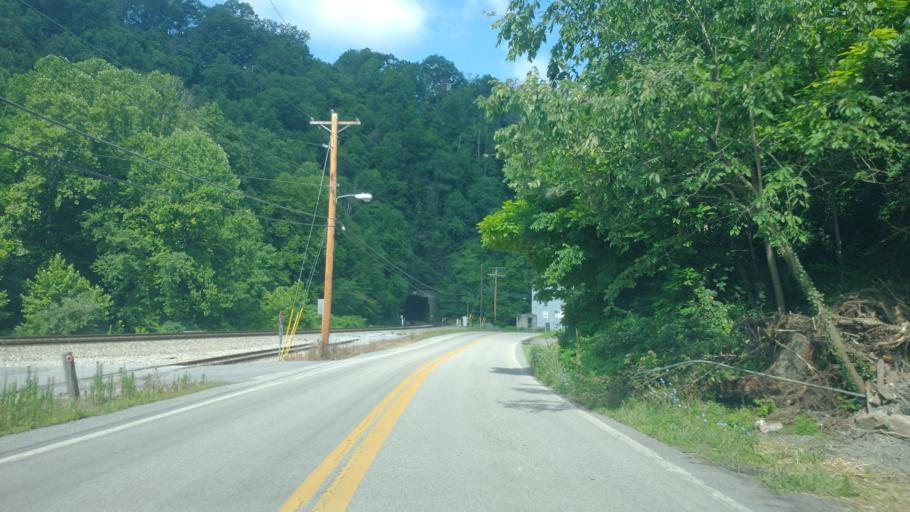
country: US
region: West Virginia
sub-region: McDowell County
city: Welch
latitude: 37.4248
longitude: -81.5053
